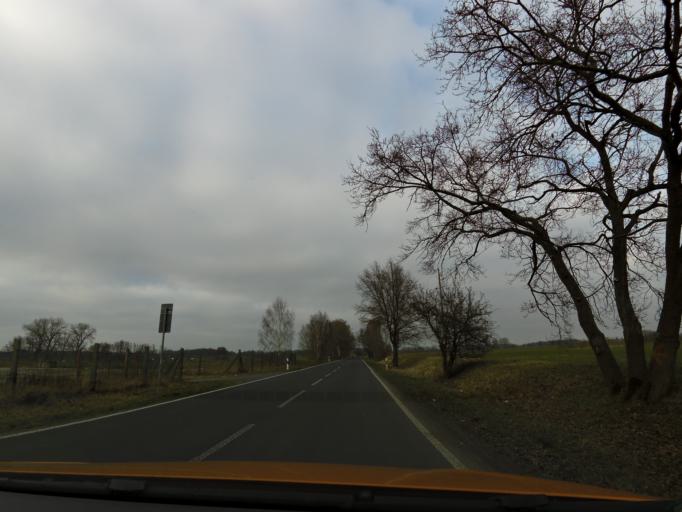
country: DE
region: Brandenburg
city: Walsleben
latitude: 52.9104
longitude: 12.6519
